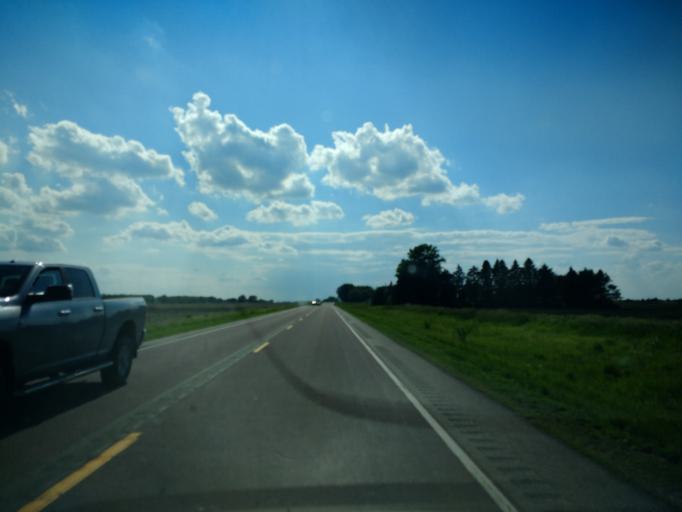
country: US
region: Iowa
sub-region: Clay County
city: Spencer
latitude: 43.1840
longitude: -95.1668
